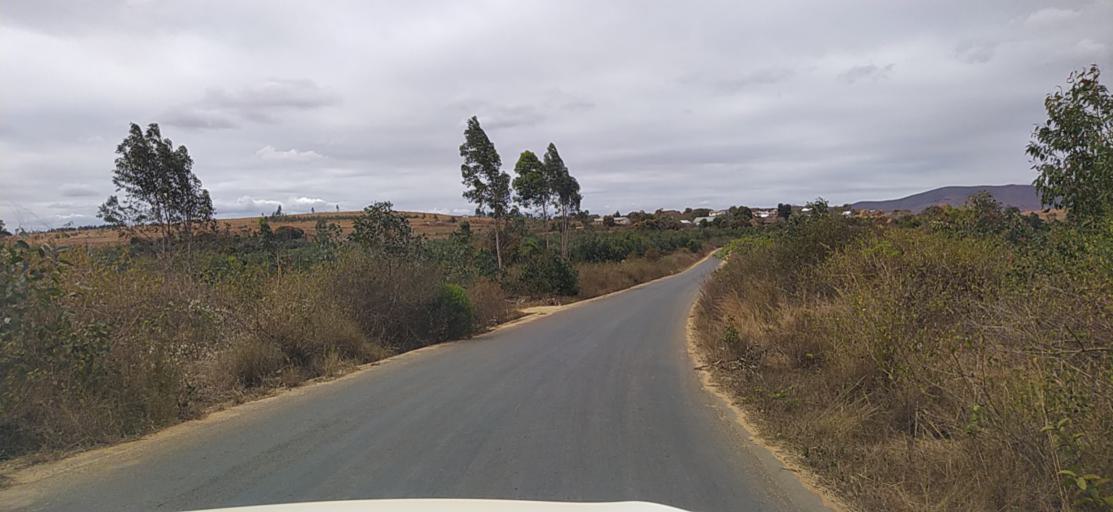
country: MG
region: Alaotra Mangoro
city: Ambatondrazaka
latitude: -17.9318
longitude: 48.2526
